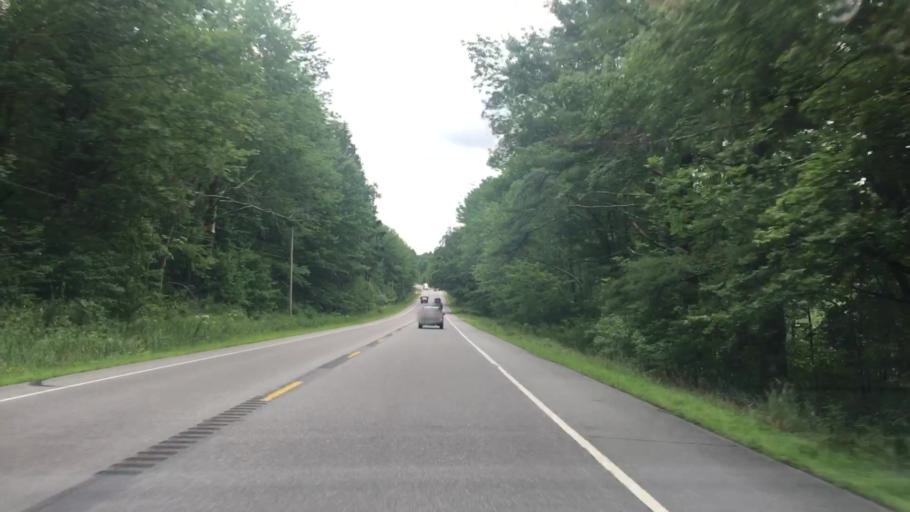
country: US
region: Maine
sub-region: York County
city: Alfred
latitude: 43.4977
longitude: -70.7188
